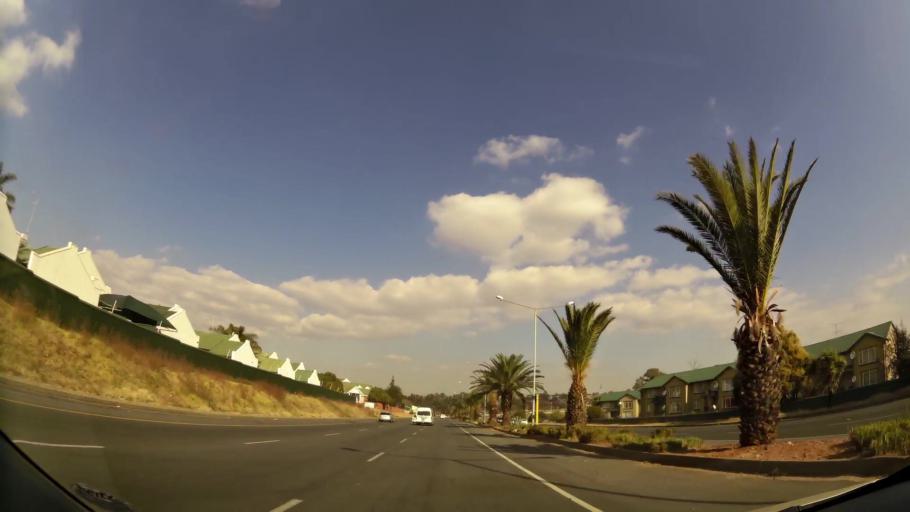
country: ZA
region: Gauteng
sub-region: West Rand District Municipality
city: Krugersdorp
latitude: -26.0957
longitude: 27.7782
